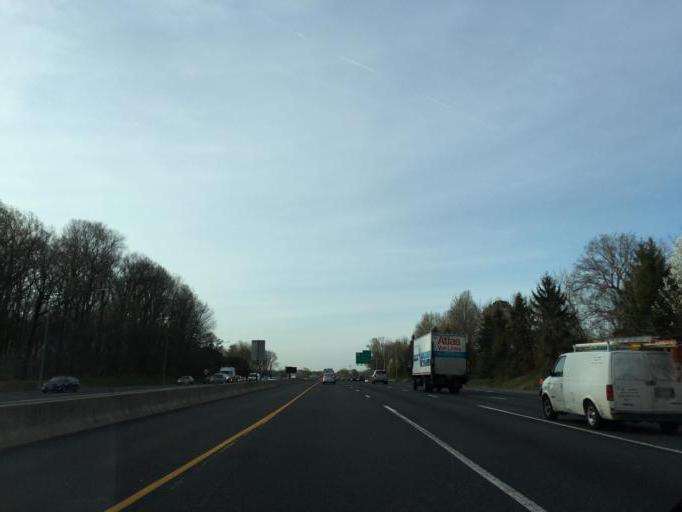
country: US
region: Maryland
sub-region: Baltimore County
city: Milford Mill
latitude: 39.3552
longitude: -76.7461
